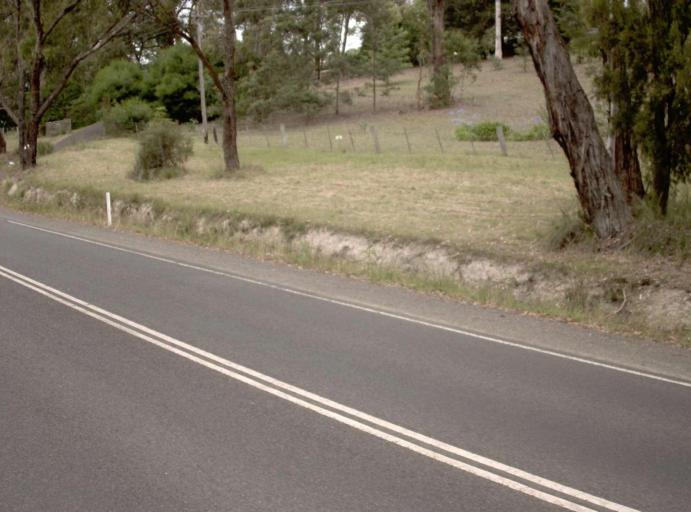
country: AU
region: Victoria
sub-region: Yarra Ranges
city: Mount Evelyn
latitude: -37.7622
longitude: 145.3996
